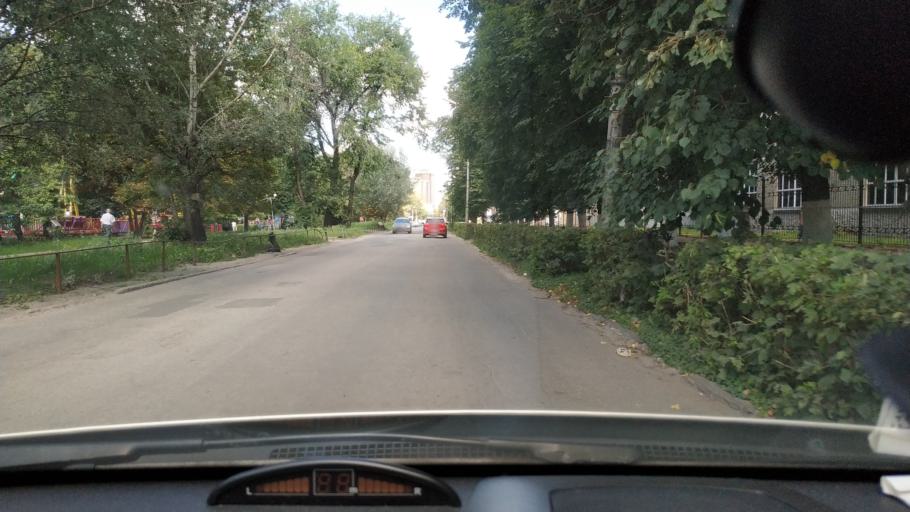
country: RU
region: Rjazan
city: Ryazan'
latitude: 54.6247
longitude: 39.7109
